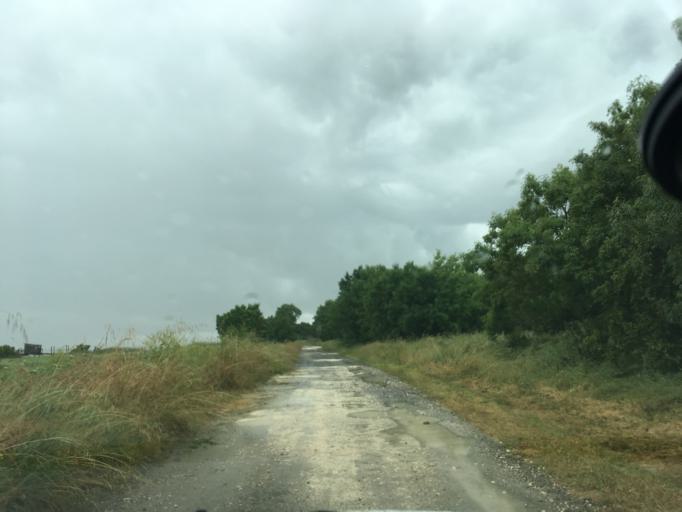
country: FR
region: Aquitaine
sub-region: Departement de la Gironde
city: Saint-Estephe
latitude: 45.3362
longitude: -0.7989
